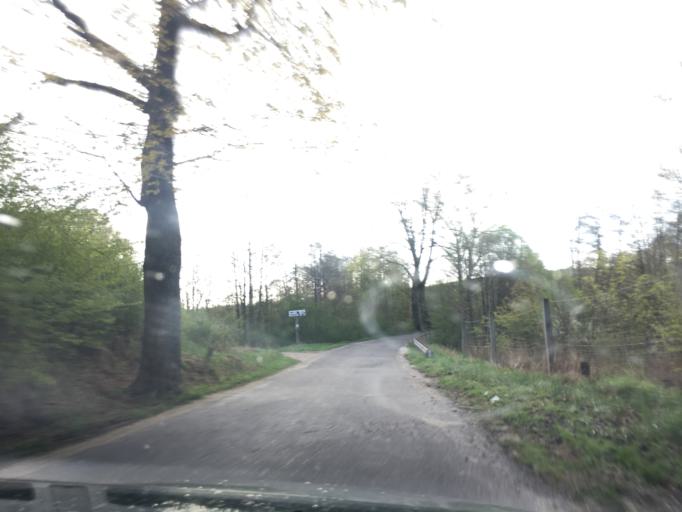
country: PL
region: Warmian-Masurian Voivodeship
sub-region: Powiat ostrodzki
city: Dabrowno
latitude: 53.4278
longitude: 20.0192
